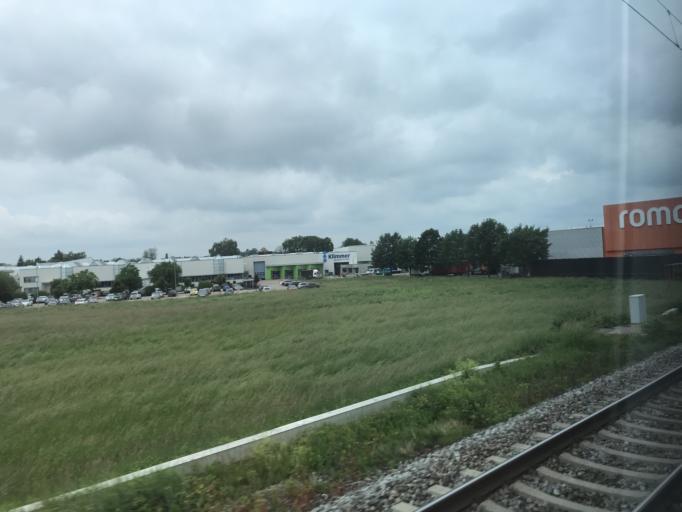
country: DE
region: Bavaria
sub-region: Swabia
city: Burgau
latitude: 48.4280
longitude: 10.4251
